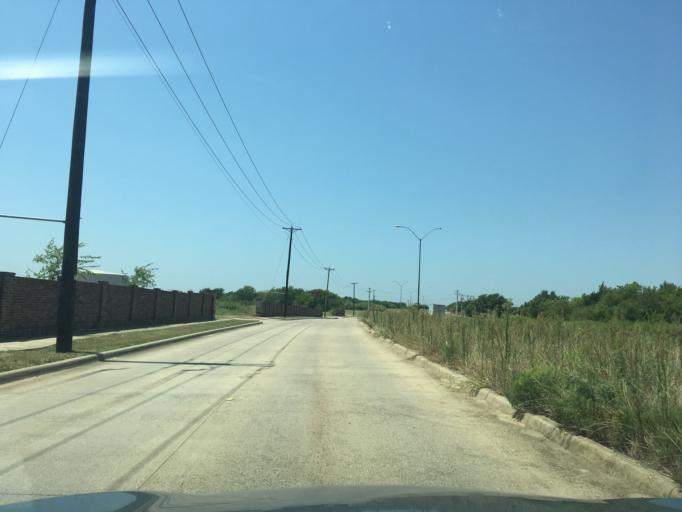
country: US
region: Texas
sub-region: Tarrant County
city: Crowley
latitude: 32.6145
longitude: -97.3672
